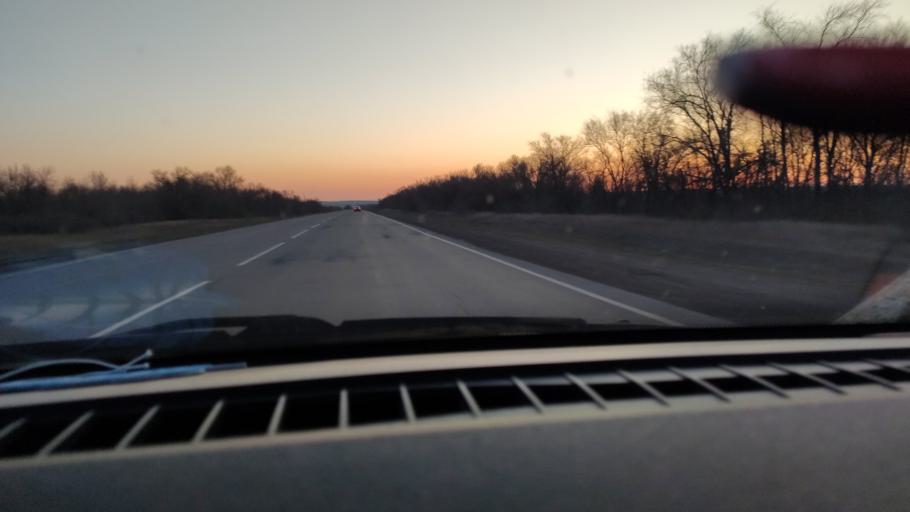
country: RU
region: Saratov
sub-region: Saratovskiy Rayon
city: Saratov
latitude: 51.7101
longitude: 46.0181
